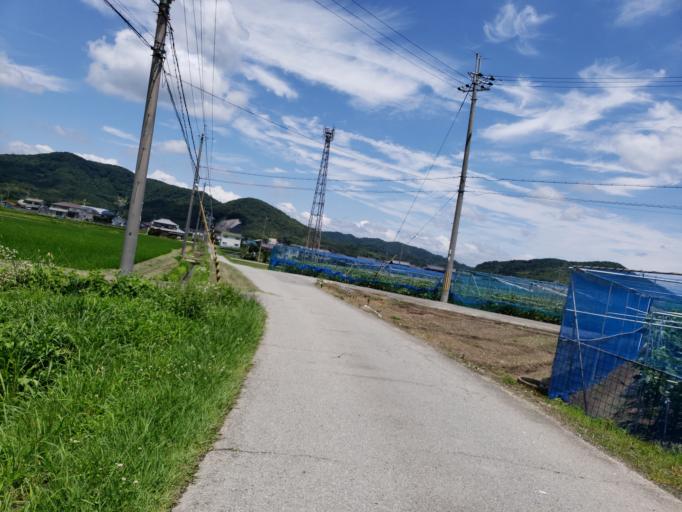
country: JP
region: Hyogo
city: Kakogawacho-honmachi
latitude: 34.8145
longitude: 134.8131
